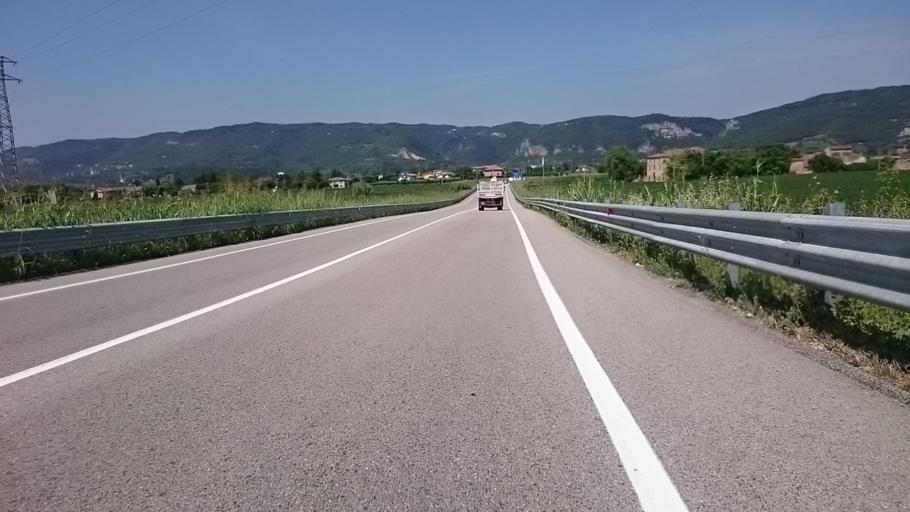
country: IT
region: Veneto
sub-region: Provincia di Vicenza
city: Villaganzerla
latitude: 45.4532
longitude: 11.6253
